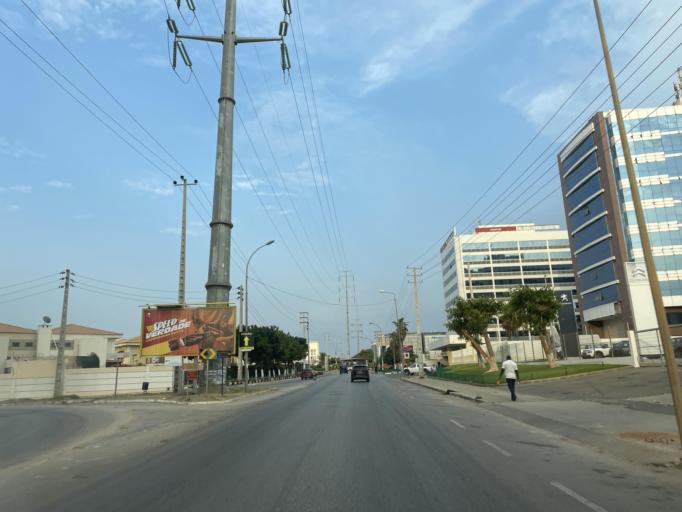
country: AO
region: Luanda
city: Luanda
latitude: -8.9218
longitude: 13.1875
